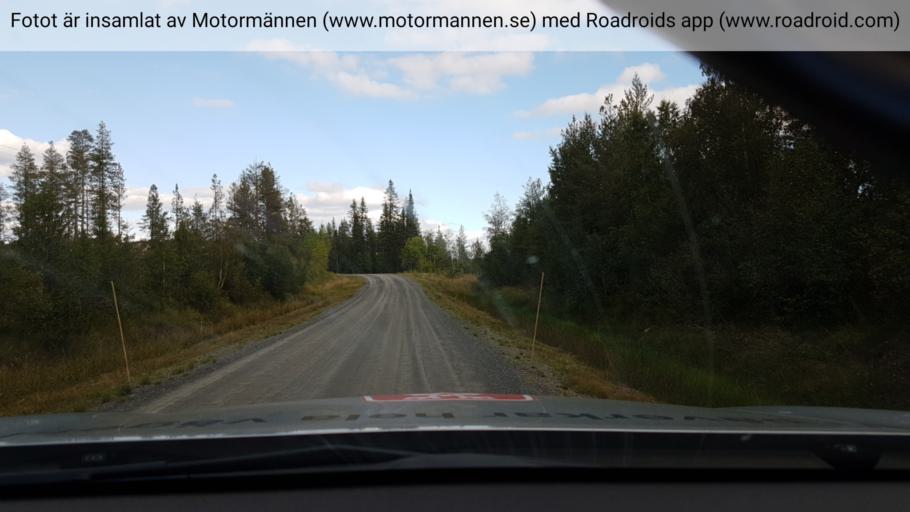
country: SE
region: Vaesterbotten
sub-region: Sorsele Kommun
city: Sorsele
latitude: 65.4553
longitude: 17.7248
